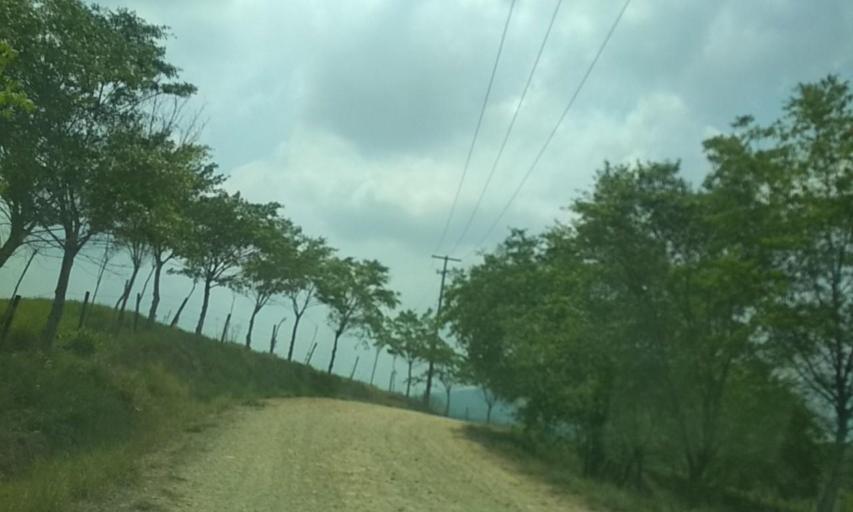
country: MX
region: Tabasco
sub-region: Huimanguillo
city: Francisco Rueda
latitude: 17.6096
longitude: -93.8079
